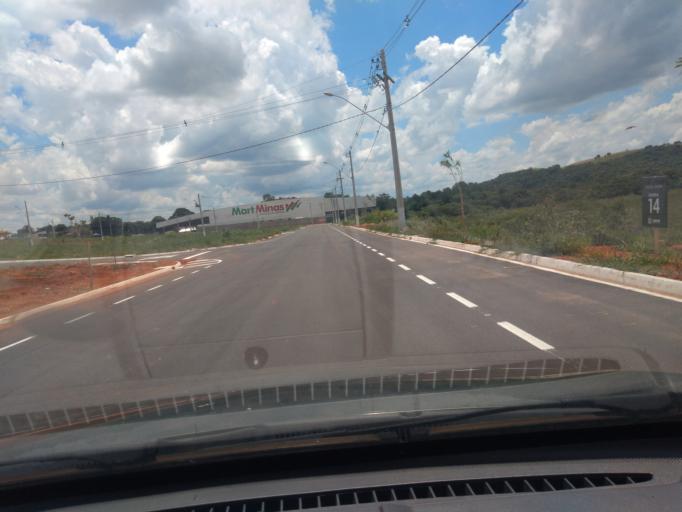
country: BR
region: Minas Gerais
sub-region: Tres Coracoes
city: Tres Coracoes
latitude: -21.6628
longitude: -45.2777
